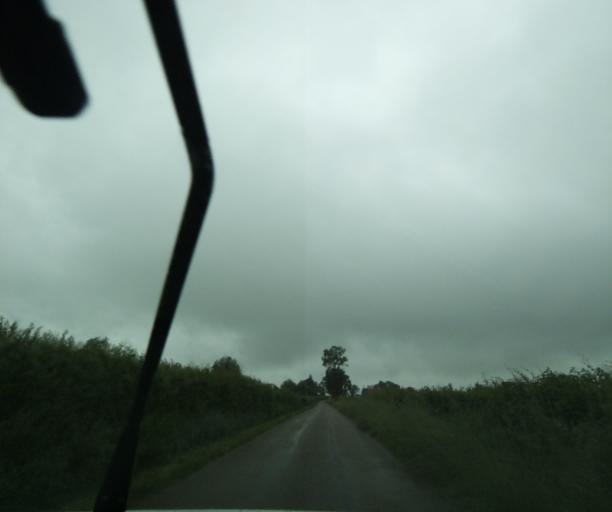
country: FR
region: Bourgogne
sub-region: Departement de Saone-et-Loire
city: Charolles
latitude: 46.3631
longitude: 4.2148
